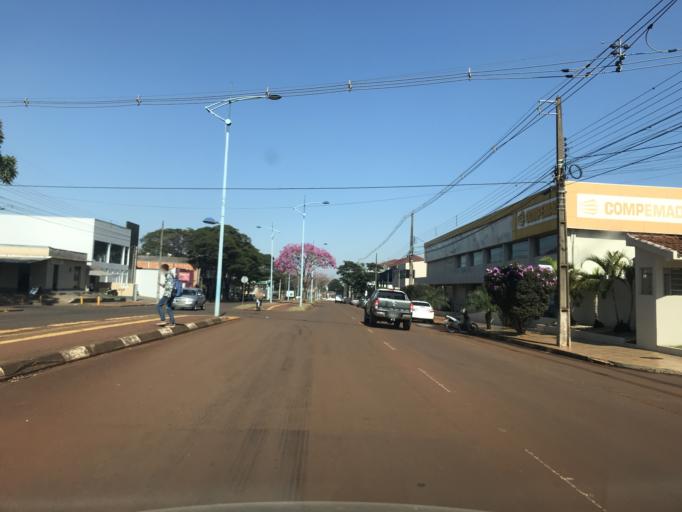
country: BR
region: Parana
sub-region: Toledo
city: Toledo
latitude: -24.7237
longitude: -53.7219
